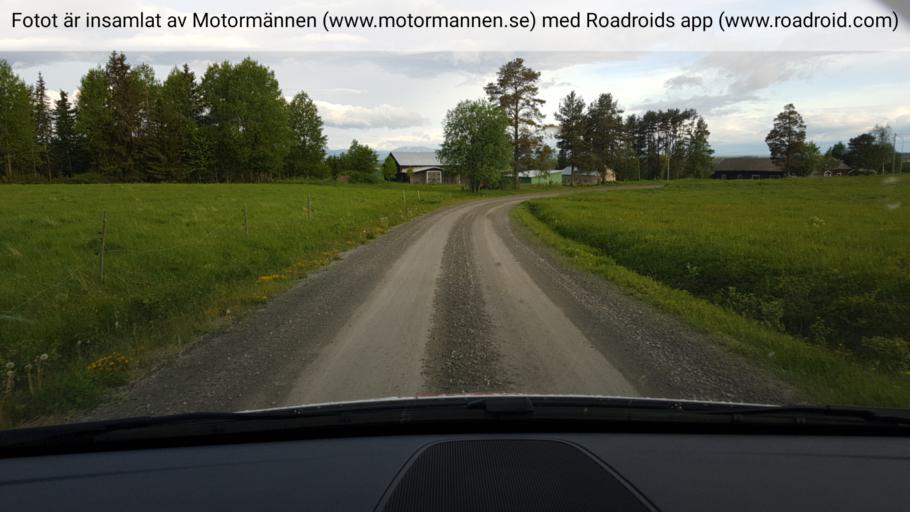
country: SE
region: Jaemtland
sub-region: Bergs Kommun
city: Hoverberg
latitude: 63.0210
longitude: 14.3758
